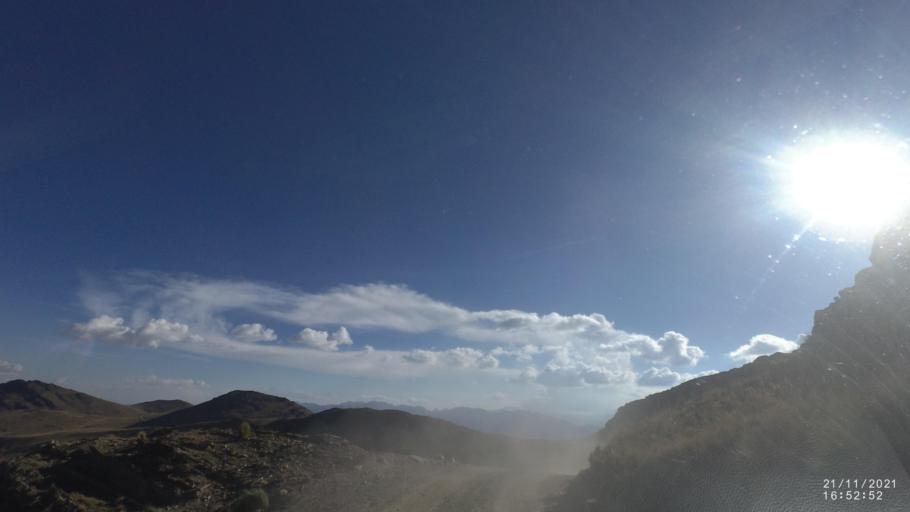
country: BO
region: Cochabamba
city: Cochabamba
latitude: -17.0846
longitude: -66.2508
